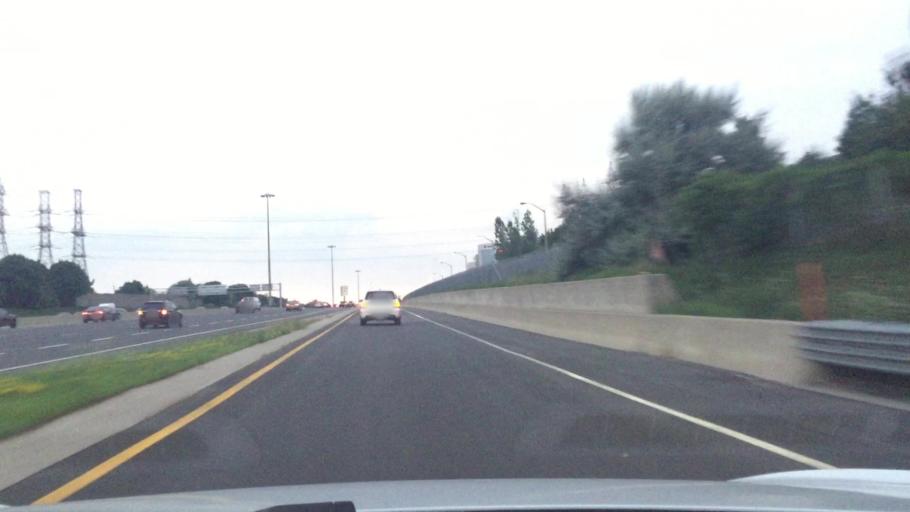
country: CA
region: Ontario
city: Willowdale
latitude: 43.7968
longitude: -79.3435
